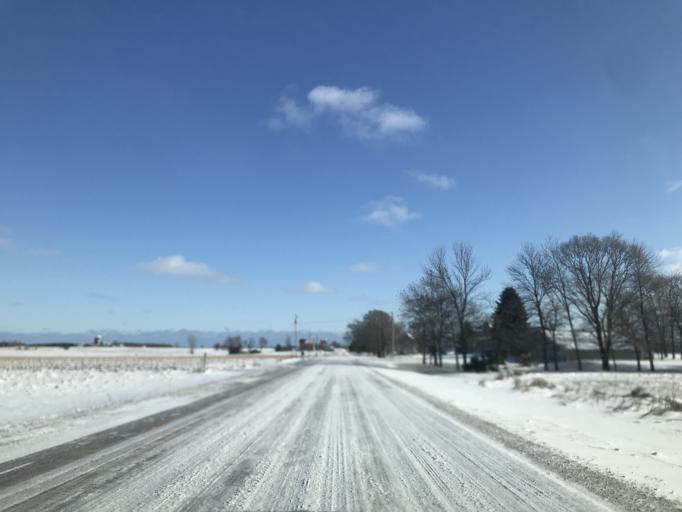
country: US
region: Wisconsin
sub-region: Kewaunee County
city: Luxemburg
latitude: 44.6977
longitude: -87.6162
